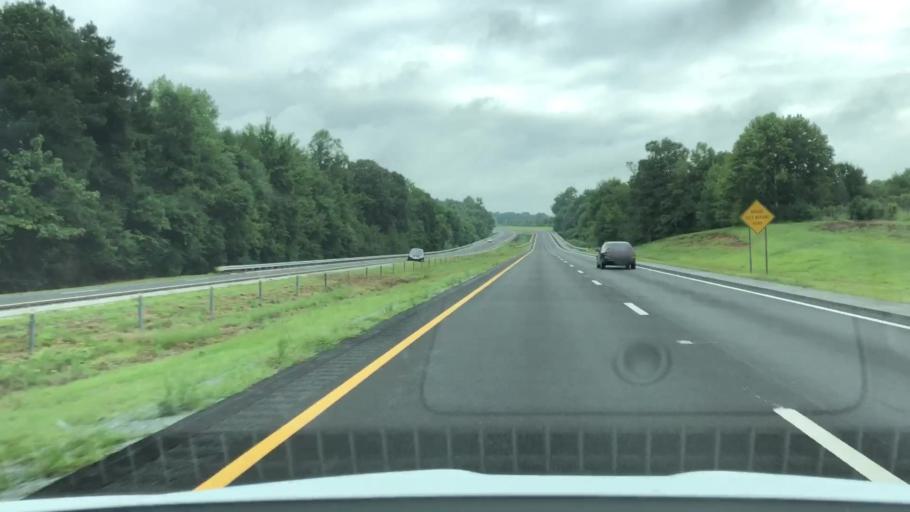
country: US
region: North Carolina
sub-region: Wayne County
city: Fremont
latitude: 35.5124
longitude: -77.9959
